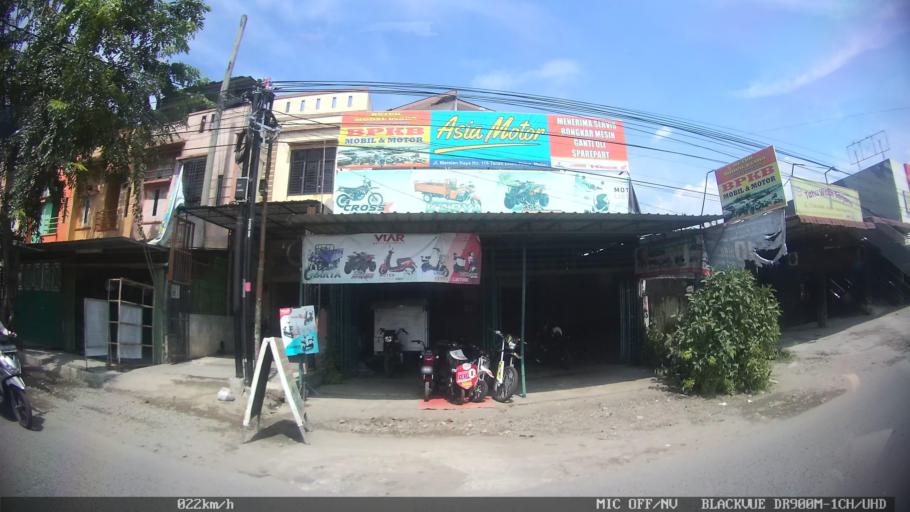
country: ID
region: North Sumatra
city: Labuhan Deli
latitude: 3.6794
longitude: 98.6560
